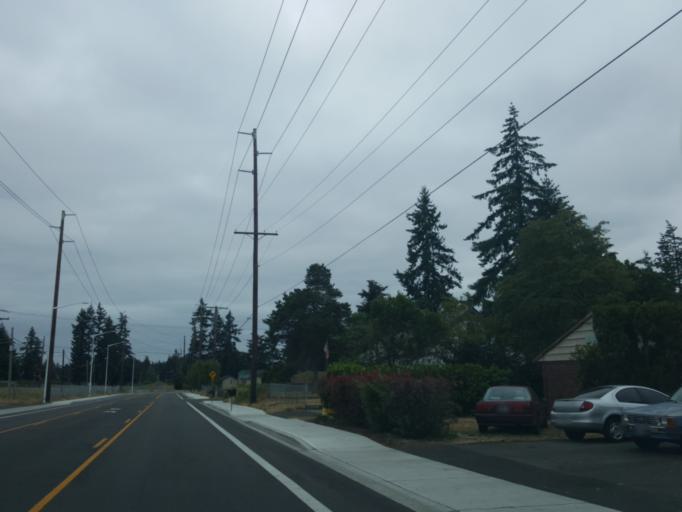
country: US
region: Washington
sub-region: Pierce County
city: McChord Air Force Base
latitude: 47.1582
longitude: -122.4954
